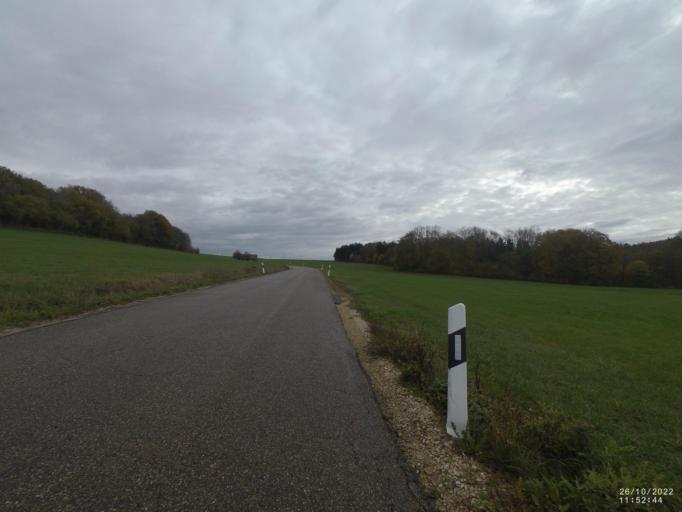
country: DE
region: Baden-Wuerttemberg
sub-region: Regierungsbezirk Stuttgart
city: Bohmenkirch
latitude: 48.6927
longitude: 9.9000
